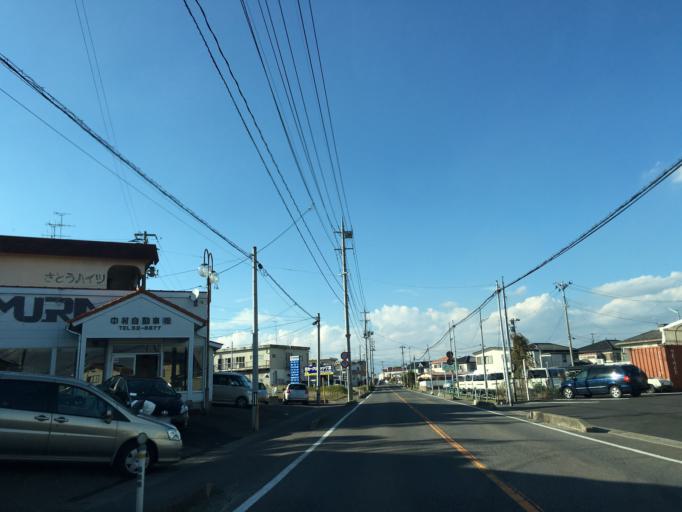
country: JP
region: Fukushima
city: Koriyama
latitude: 37.4114
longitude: 140.3342
